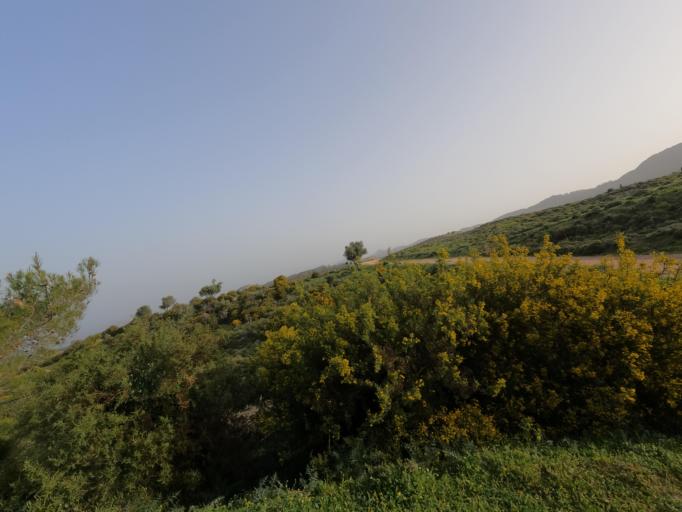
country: CY
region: Pafos
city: Pegeia
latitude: 34.9810
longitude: 32.3283
